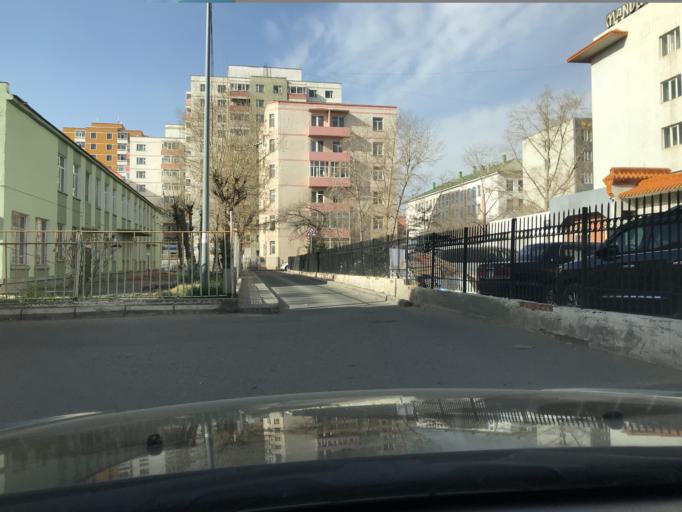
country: MN
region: Ulaanbaatar
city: Ulaanbaatar
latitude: 47.9175
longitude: 106.9039
